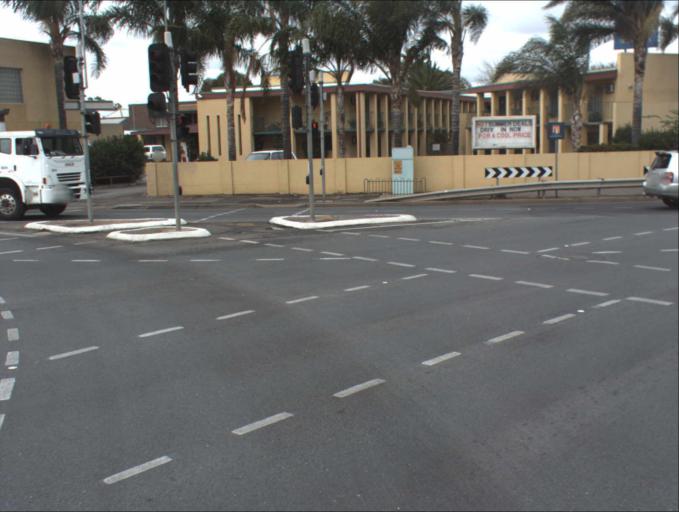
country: AU
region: South Australia
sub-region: Prospect
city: Prospect
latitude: -34.8935
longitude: 138.6033
